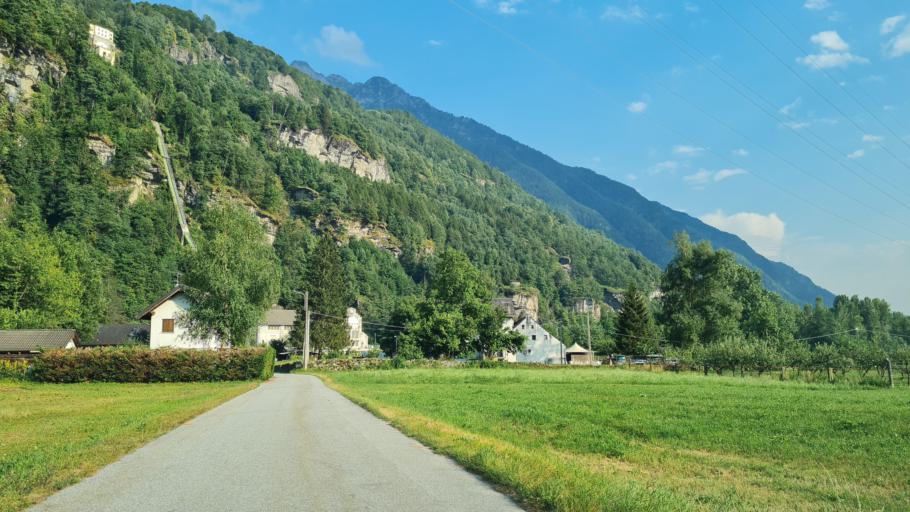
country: IT
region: Piedmont
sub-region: Provincia Verbano-Cusio-Ossola
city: Baceno
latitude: 46.2489
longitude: 8.3294
